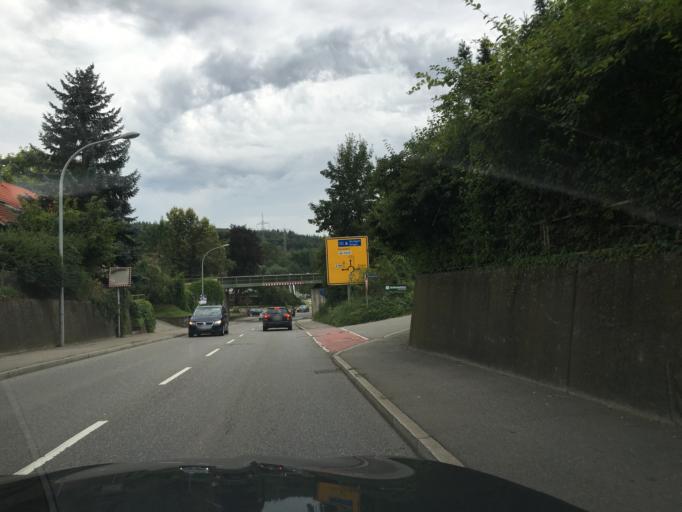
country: DE
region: Baden-Wuerttemberg
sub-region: Freiburg Region
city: Stockach
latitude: 47.8432
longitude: 8.9960
